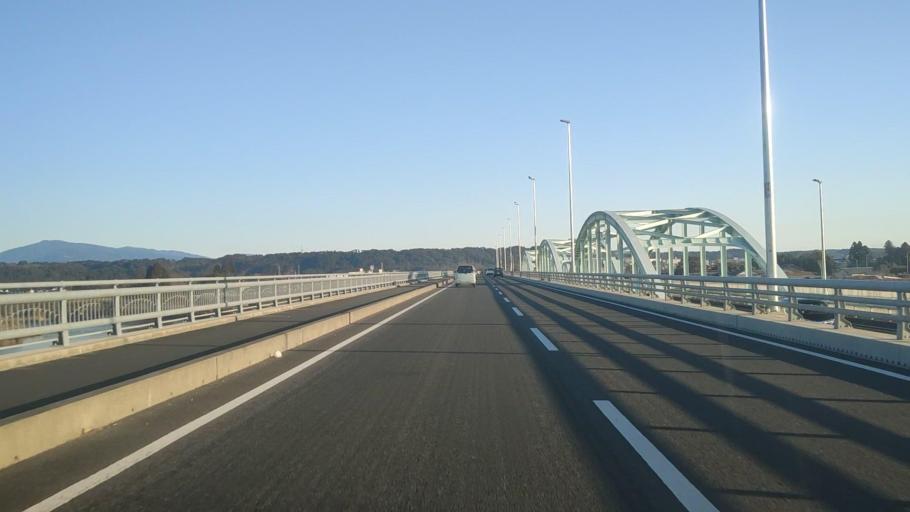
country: JP
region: Miyazaki
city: Takanabe
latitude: 32.0498
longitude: 131.4724
